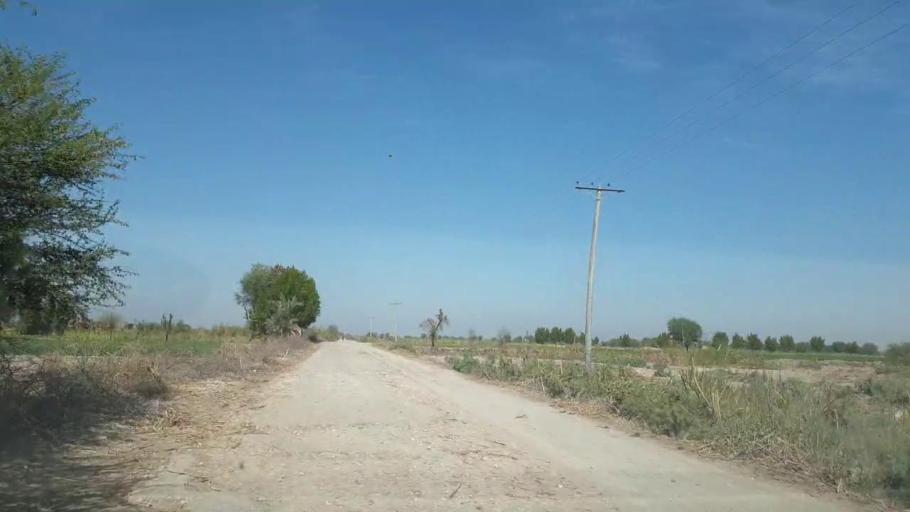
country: PK
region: Sindh
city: Pithoro
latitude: 25.6142
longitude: 69.2163
